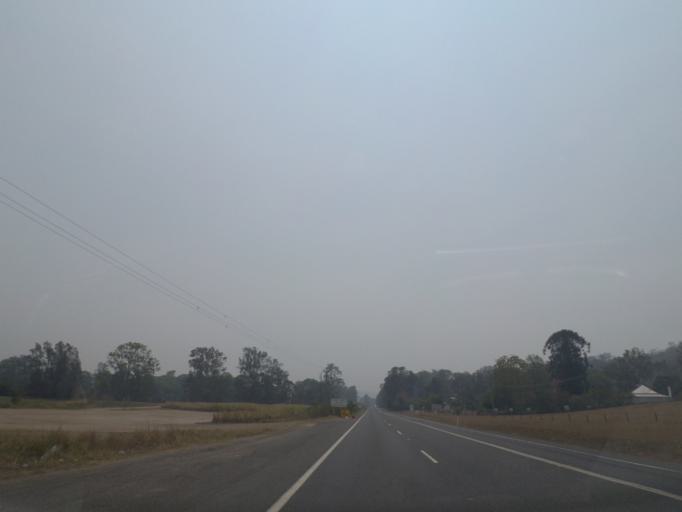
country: AU
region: New South Wales
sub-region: Clarence Valley
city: Maclean
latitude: -29.5607
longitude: 153.1491
